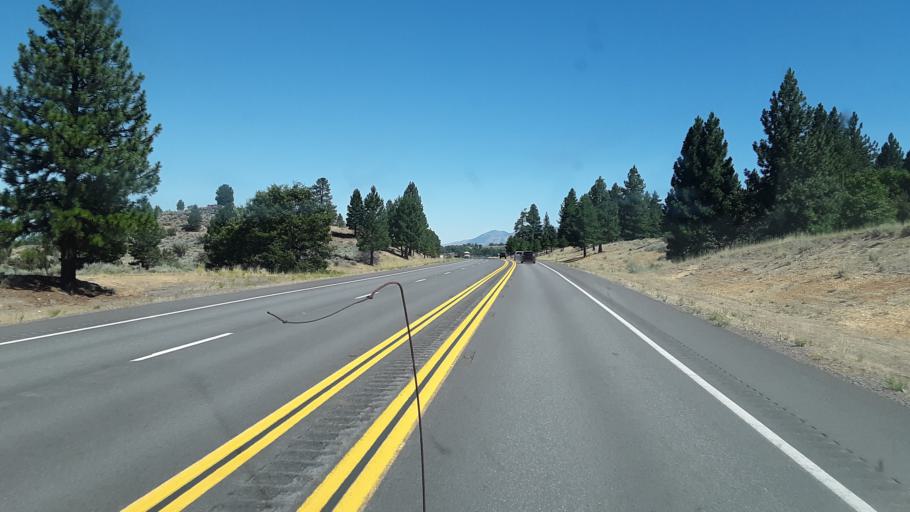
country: US
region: California
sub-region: Lassen County
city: Janesville
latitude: 40.3066
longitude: -120.5295
